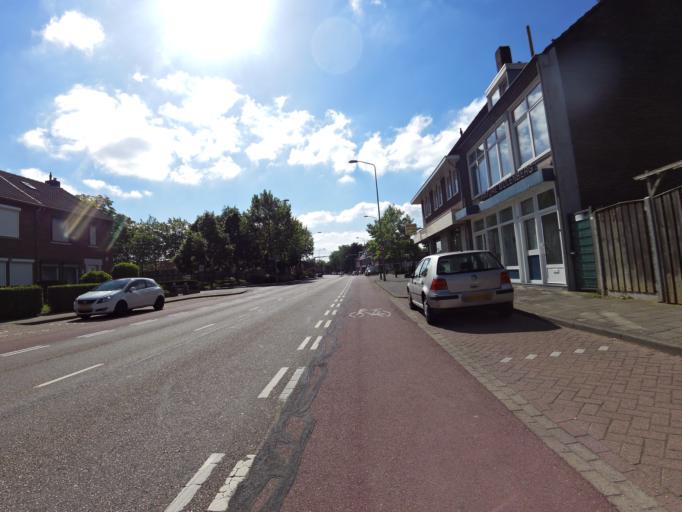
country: NL
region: Limburg
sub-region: Gemeente Heerlen
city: Heerlen
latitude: 50.8835
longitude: 5.9967
